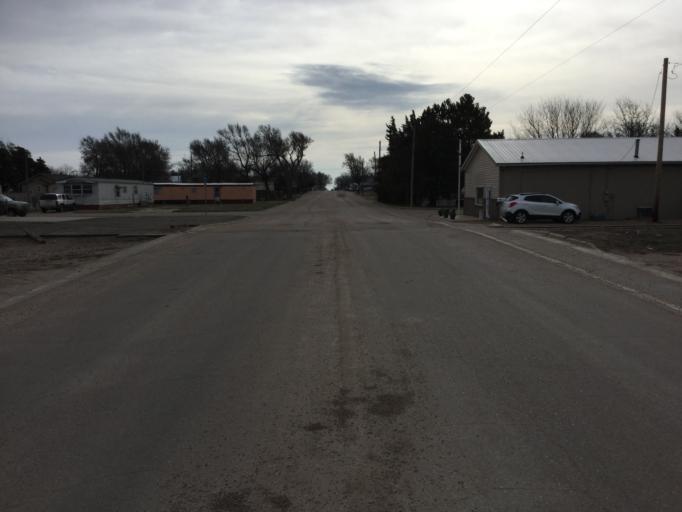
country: US
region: Kansas
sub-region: Scott County
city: Scott City
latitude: 38.4784
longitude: -100.9126
